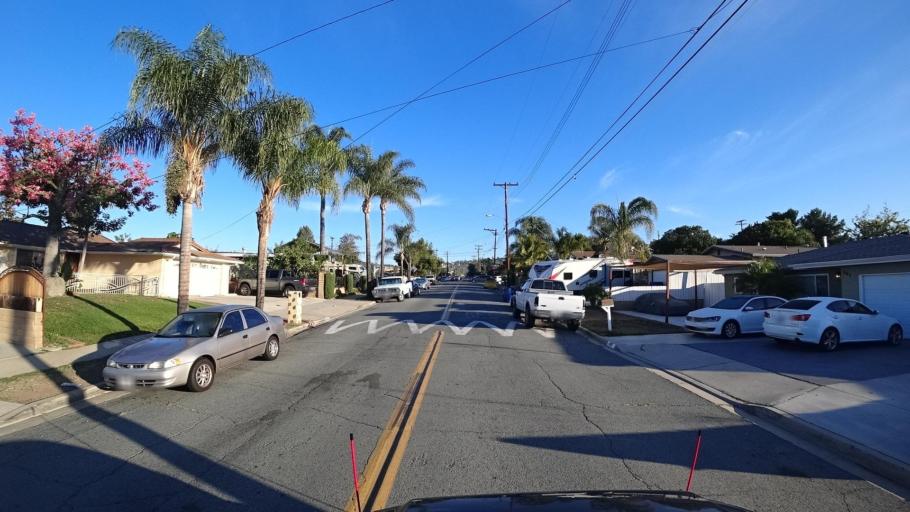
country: US
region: California
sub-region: San Diego County
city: La Presa
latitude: 32.7092
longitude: -117.0018
